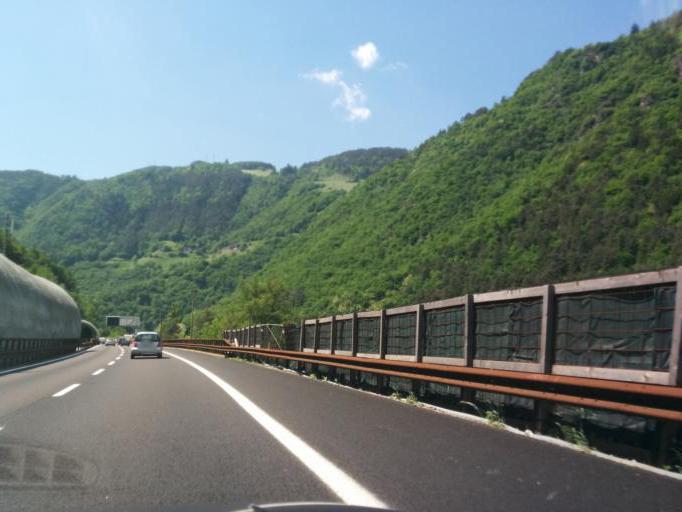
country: IT
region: Trentino-Alto Adige
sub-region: Bolzano
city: Ponte Gardena
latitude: 46.5643
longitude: 11.5170
